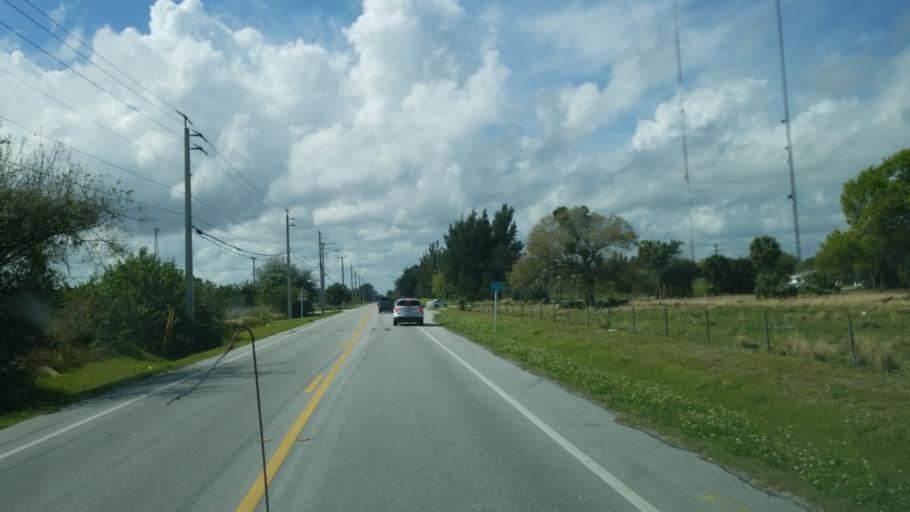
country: US
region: Florida
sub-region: Saint Lucie County
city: Lakewood Park
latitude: 27.4475
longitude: -80.4061
